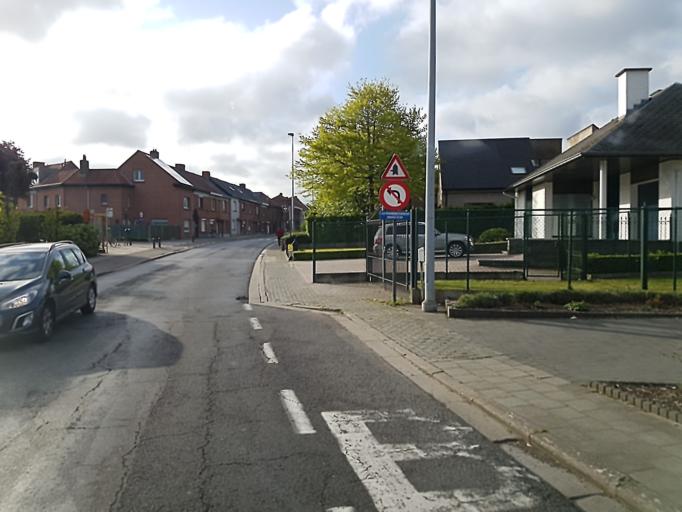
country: BE
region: Flanders
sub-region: Provincie Oost-Vlaanderen
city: Temse
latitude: 51.1300
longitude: 4.1949
